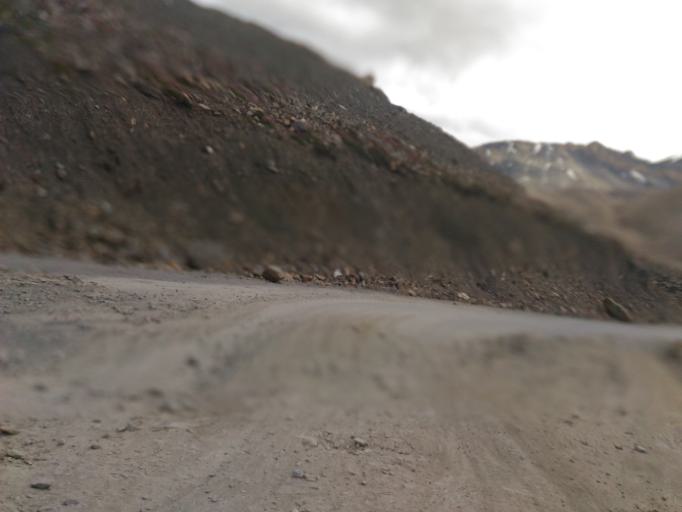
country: IN
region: Himachal Pradesh
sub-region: Lahul and Spiti
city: Kyelang
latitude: 32.7704
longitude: 77.3786
